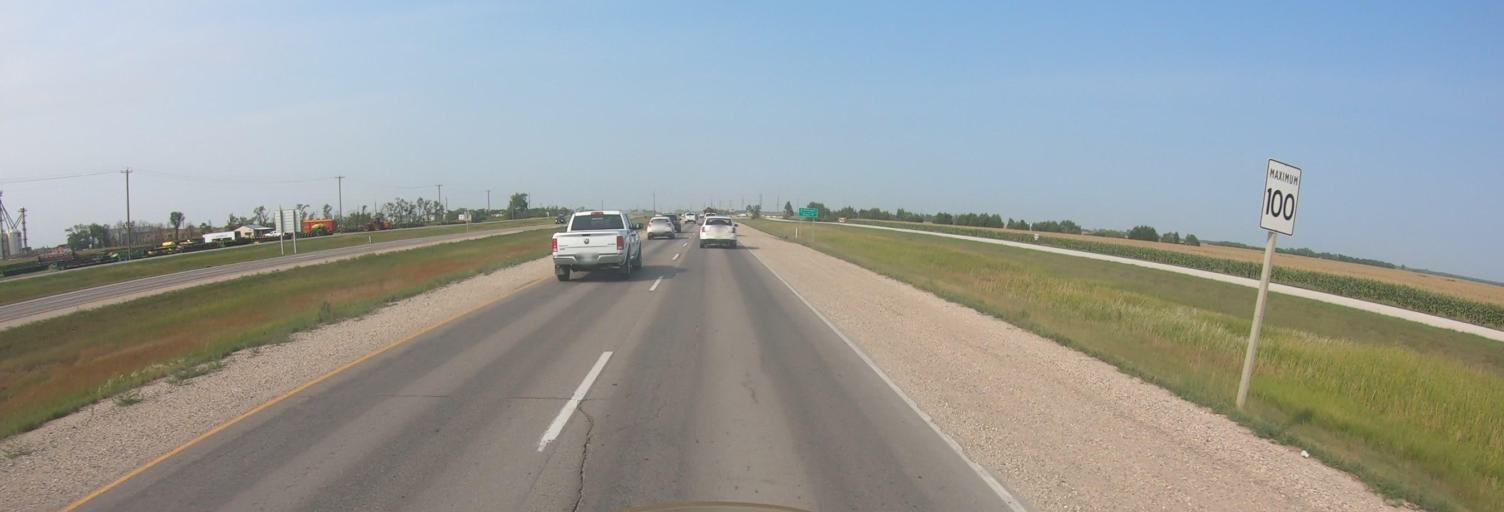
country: CA
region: Manitoba
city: Steinbach
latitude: 49.5706
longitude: -96.6873
